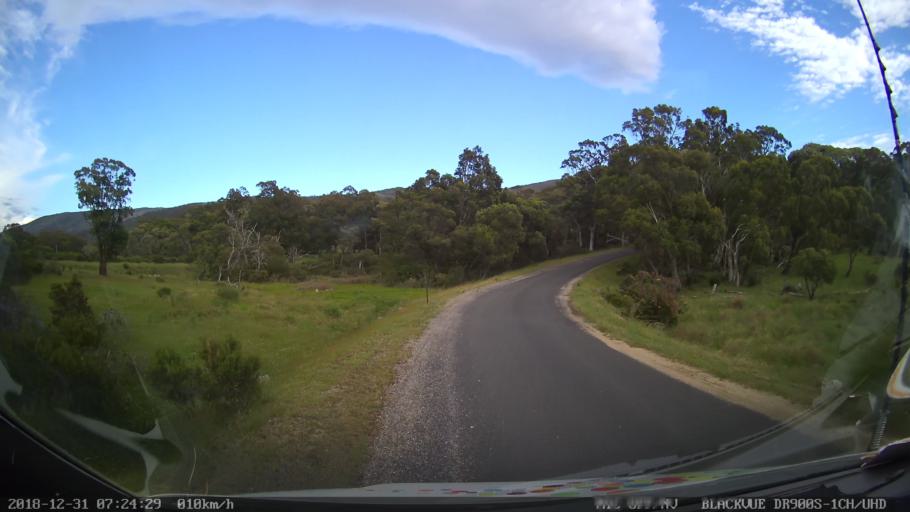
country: AU
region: New South Wales
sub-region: Snowy River
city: Jindabyne
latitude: -36.3235
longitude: 148.4748
